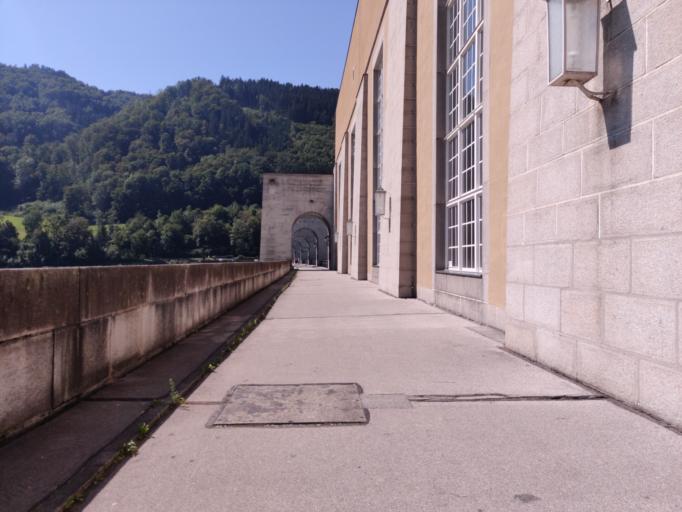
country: DE
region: Bavaria
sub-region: Lower Bavaria
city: Untergriesbach
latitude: 48.5182
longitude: 13.7075
